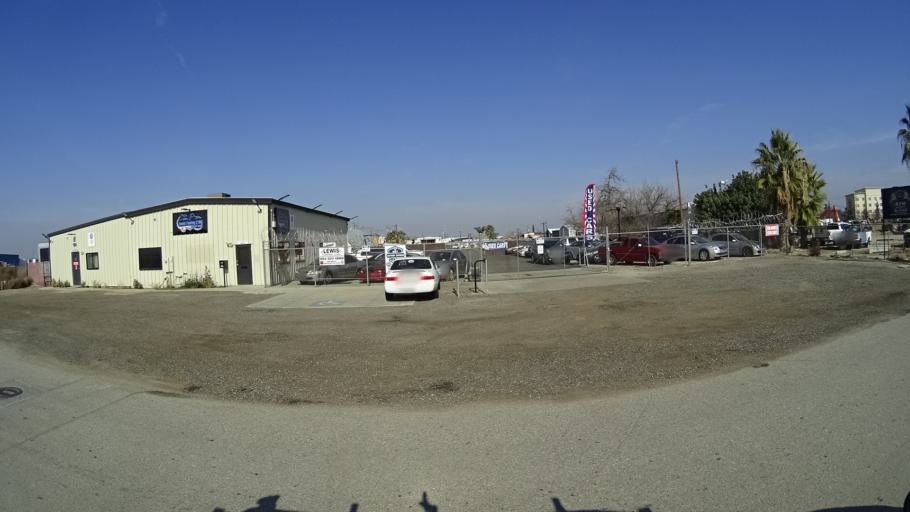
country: US
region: California
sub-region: Kern County
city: Bakersfield
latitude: 35.3786
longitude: -119.0539
